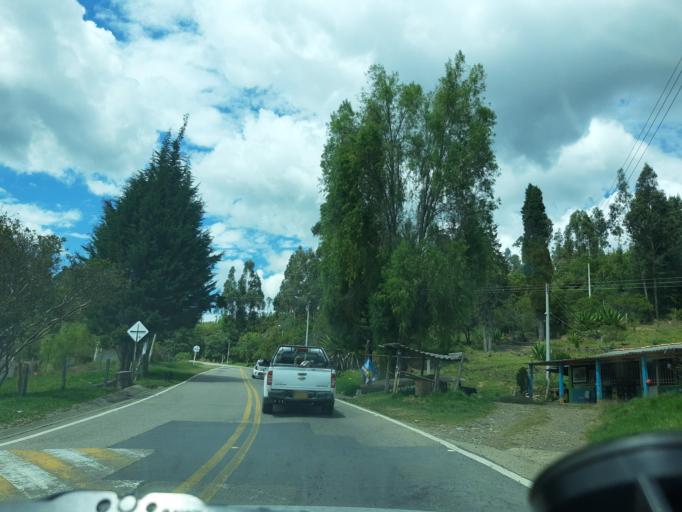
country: CO
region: Boyaca
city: Raquira
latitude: 5.5773
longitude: -73.6850
